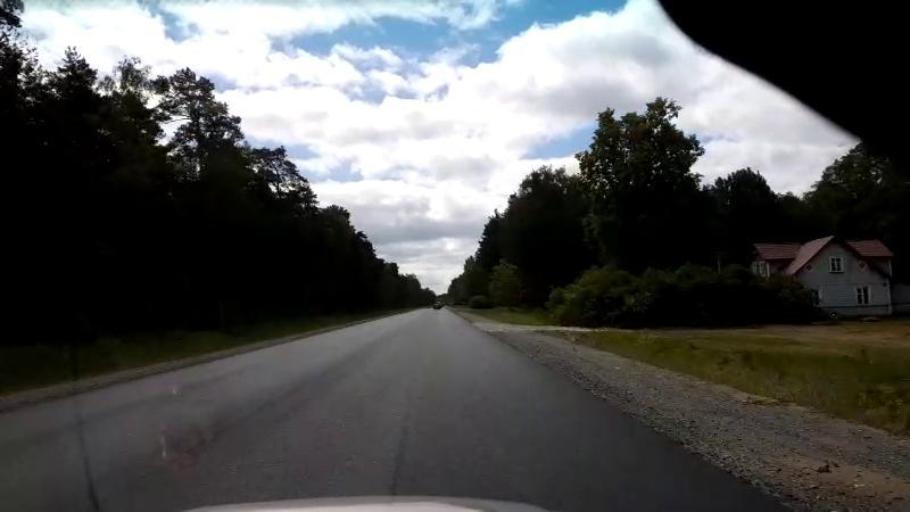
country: LV
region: Salacgrivas
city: Salacgriva
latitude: 57.8029
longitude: 24.3492
